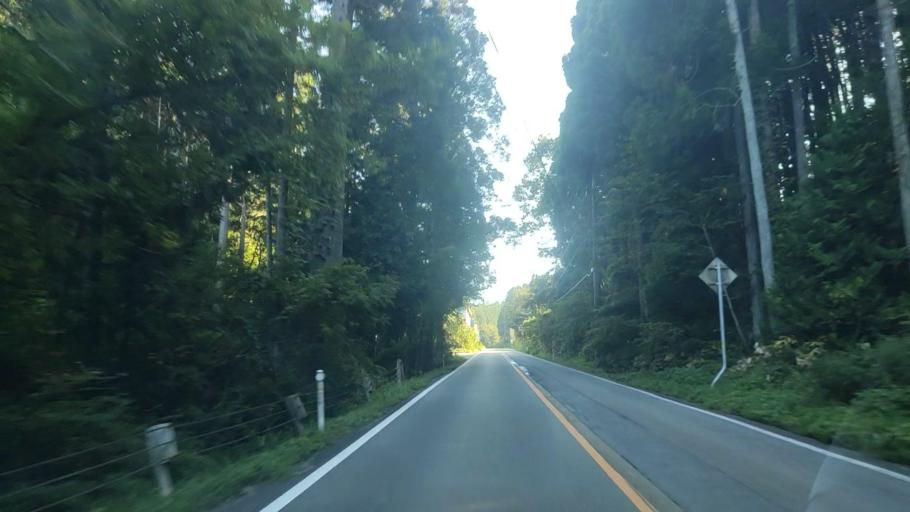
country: JP
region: Ishikawa
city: Nanao
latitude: 37.1363
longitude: 136.8629
